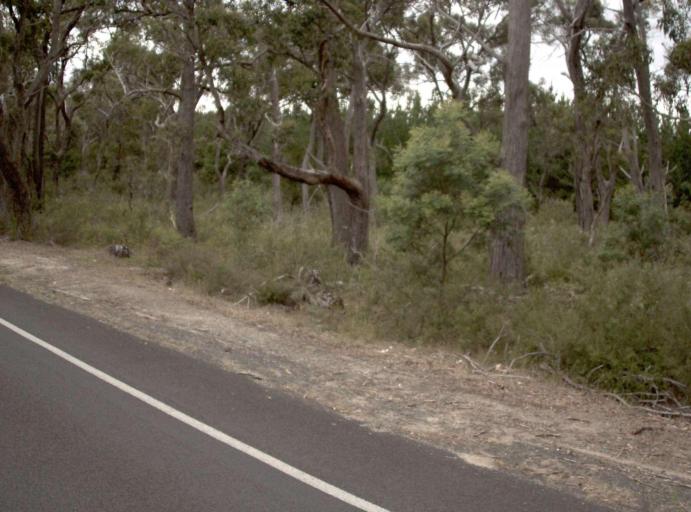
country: AU
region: Victoria
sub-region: Wellington
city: Sale
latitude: -38.2279
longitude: 147.0552
